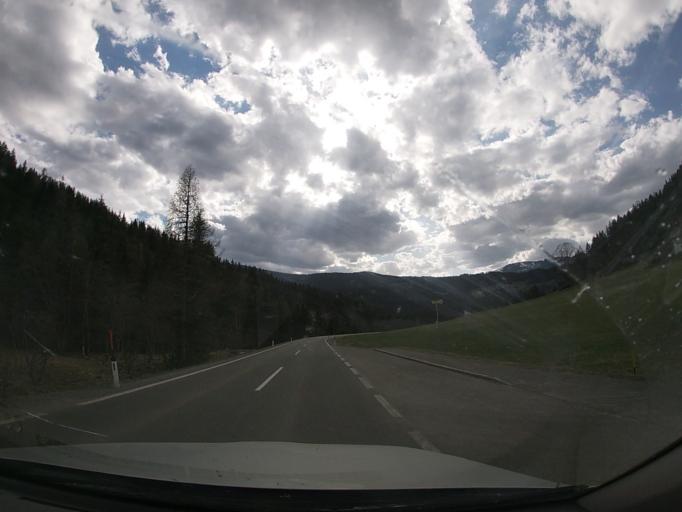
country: AT
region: Styria
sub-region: Politischer Bezirk Murau
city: Triebendorf
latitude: 47.0573
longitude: 14.2331
